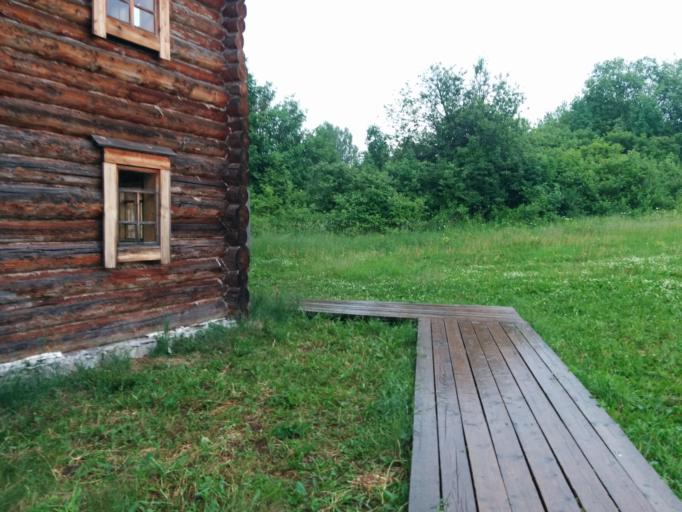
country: RU
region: Perm
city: Polazna
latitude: 58.2590
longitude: 56.2601
